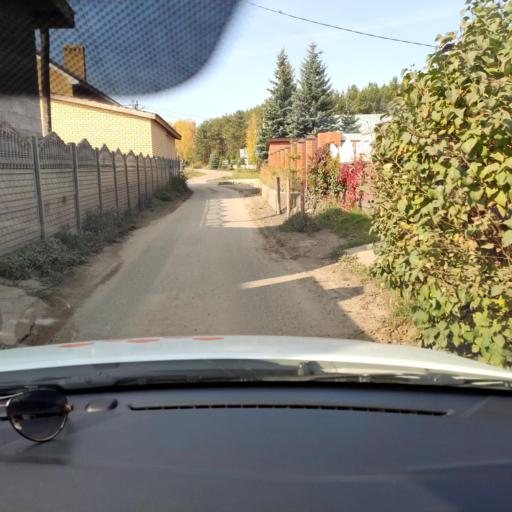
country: RU
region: Tatarstan
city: Stolbishchi
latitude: 55.6790
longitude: 49.1167
